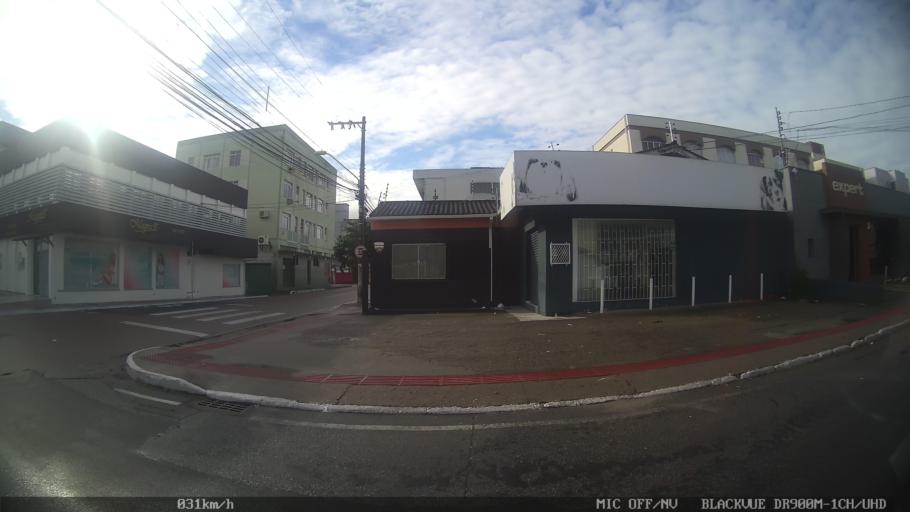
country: BR
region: Santa Catarina
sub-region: Sao Jose
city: Campinas
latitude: -27.6008
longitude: -48.6163
